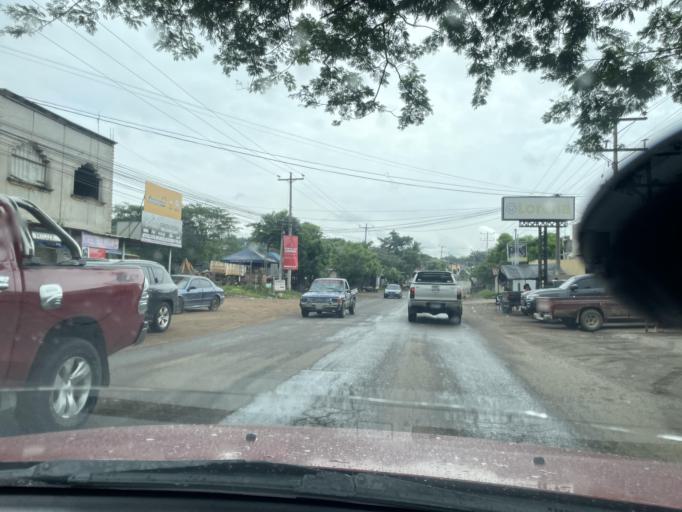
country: SV
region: La Union
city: Santa Rosa de Lima
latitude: 13.6276
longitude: -87.8931
